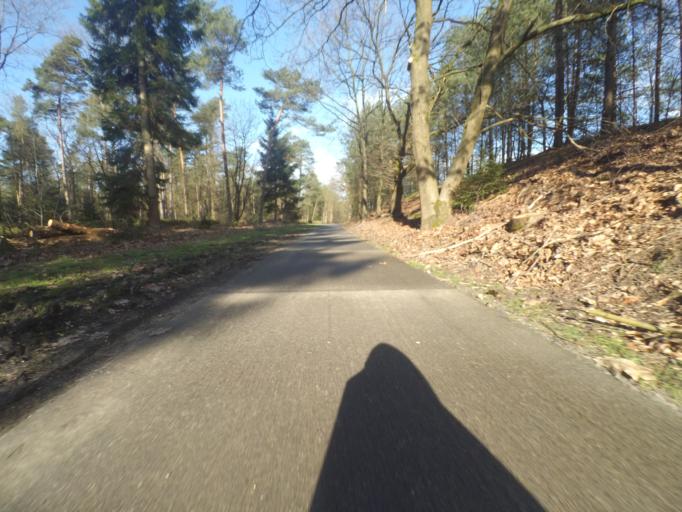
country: NL
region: Gelderland
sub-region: Gemeente Apeldoorn
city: Beekbergen
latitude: 52.1928
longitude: 5.8824
